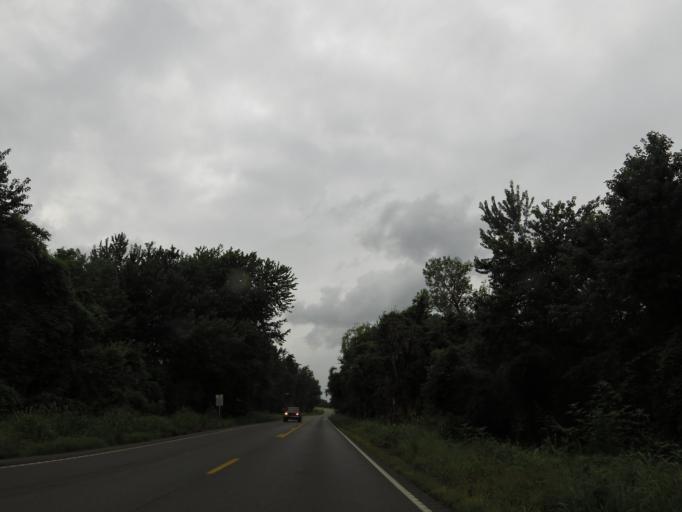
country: US
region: Illinois
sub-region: Alexander County
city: Cairo
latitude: 36.9997
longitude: -89.1337
